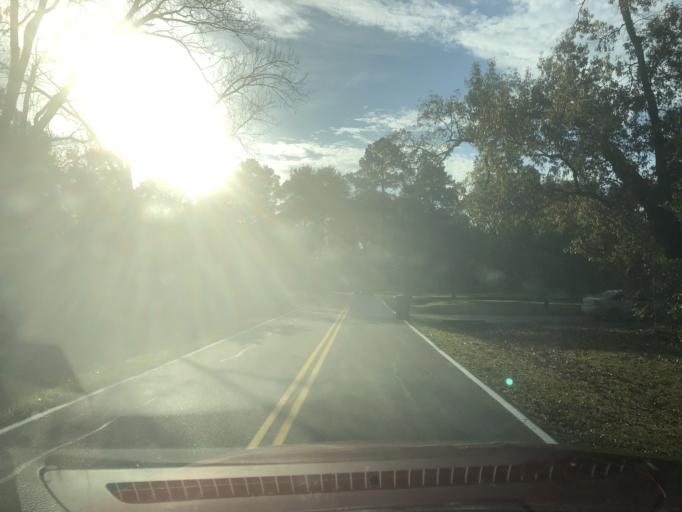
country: US
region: Texas
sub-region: Harris County
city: Spring
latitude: 30.0096
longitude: -95.4741
